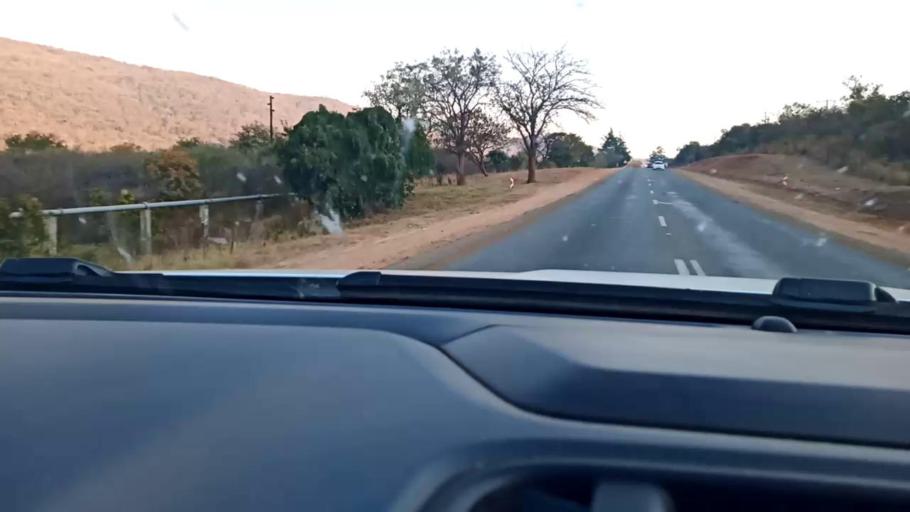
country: ZA
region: Limpopo
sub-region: Mopani District Municipality
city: Duiwelskloof
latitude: -23.6565
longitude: 30.1694
